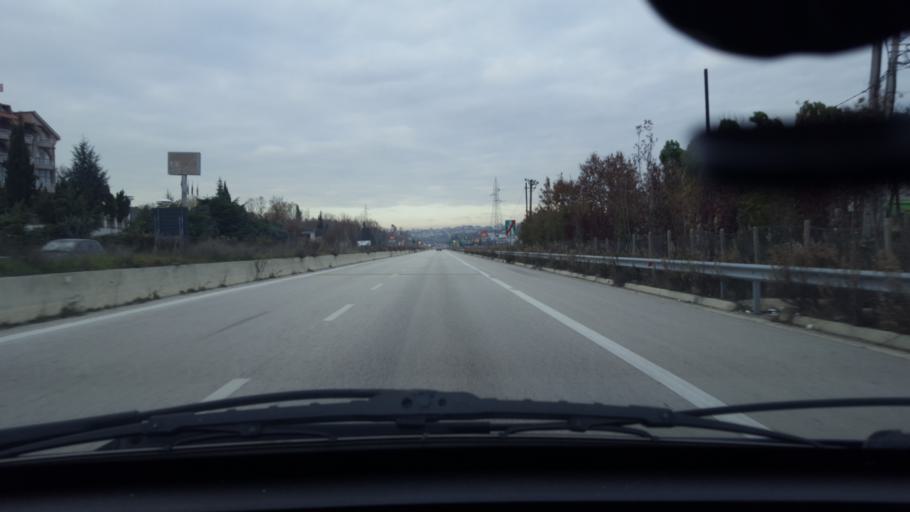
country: AL
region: Tirane
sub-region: Rrethi i Tiranes
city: Petrele
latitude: 41.2786
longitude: 19.8555
